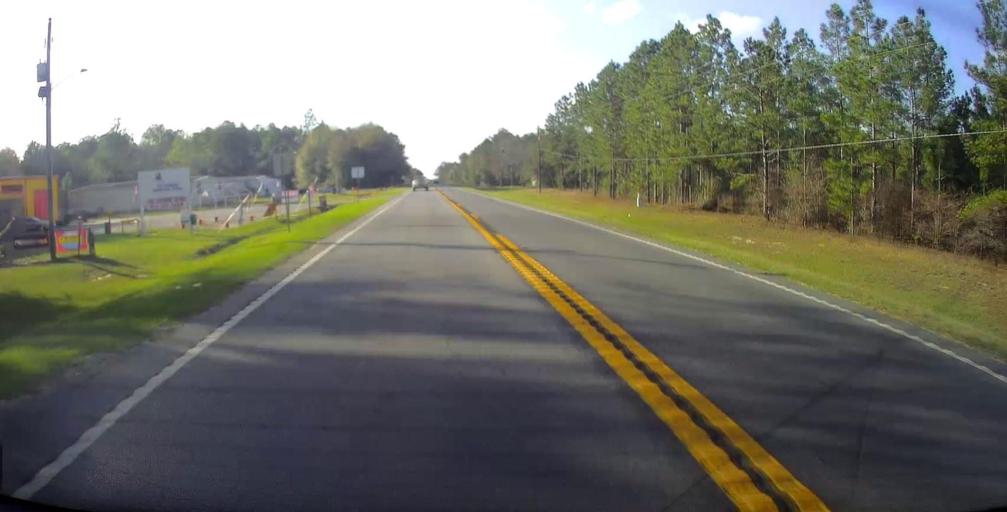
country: US
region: Georgia
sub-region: Tattnall County
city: Reidsville
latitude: 32.0831
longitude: -82.1367
